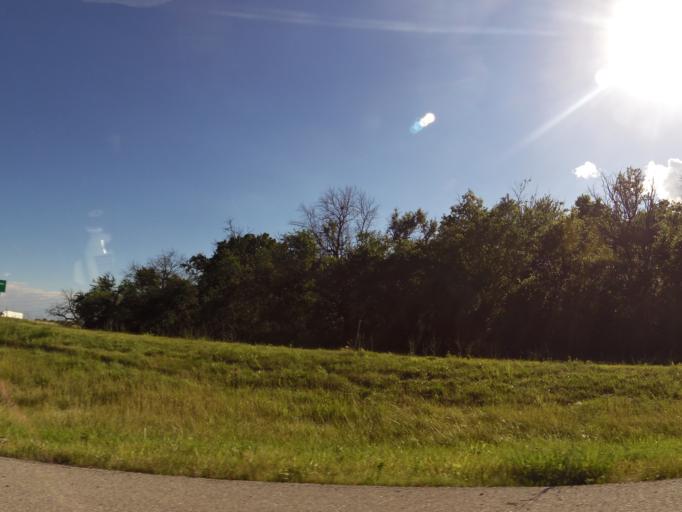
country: US
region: Missouri
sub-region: Ralls County
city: New London
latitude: 39.5757
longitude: -91.4019
